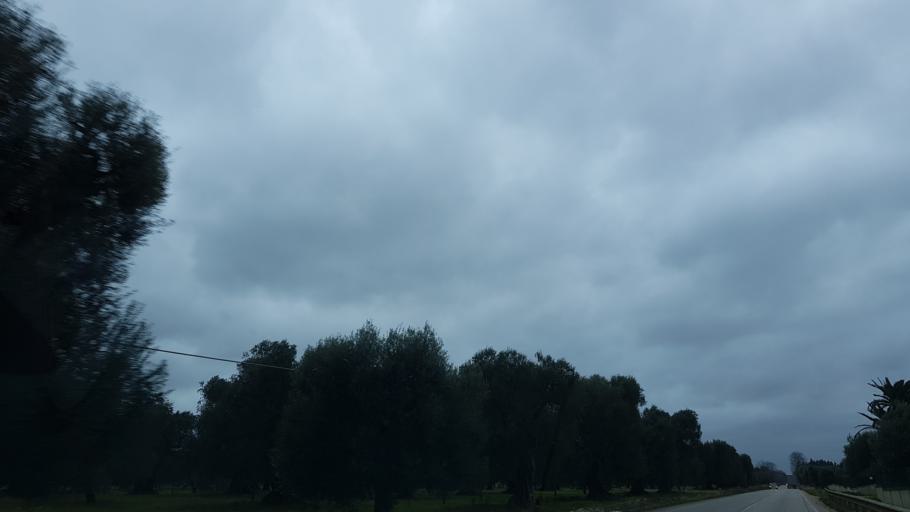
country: IT
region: Apulia
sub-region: Provincia di Brindisi
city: San Vito dei Normanni
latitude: 40.6554
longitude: 17.7540
